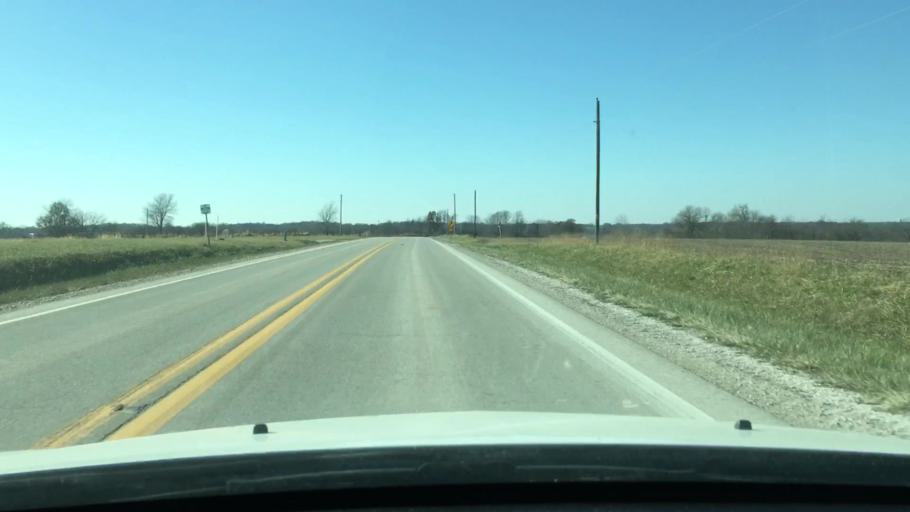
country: US
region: Illinois
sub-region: Pike County
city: Pittsfield
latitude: 39.6168
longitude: -90.7286
